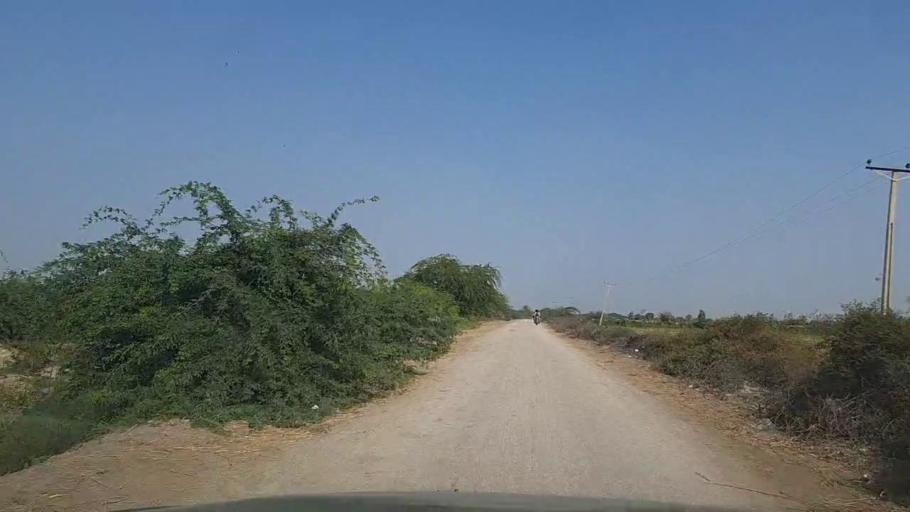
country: PK
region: Sindh
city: Thatta
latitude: 24.5965
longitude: 67.9504
